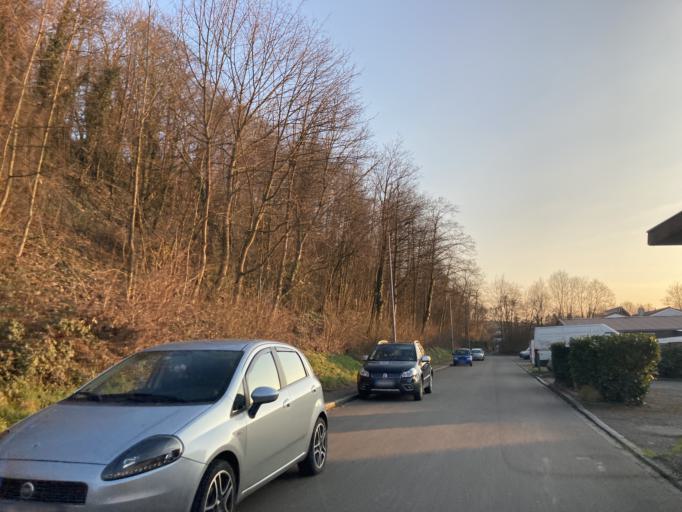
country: DE
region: Baden-Wuerttemberg
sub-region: Freiburg Region
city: Mullheim
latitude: 47.8138
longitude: 7.6145
